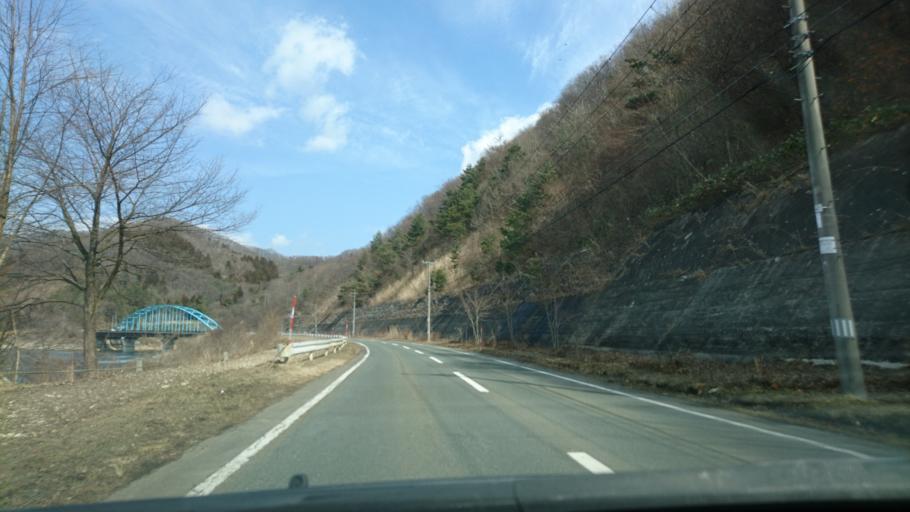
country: JP
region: Iwate
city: Shizukuishi
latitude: 39.6852
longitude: 141.0317
